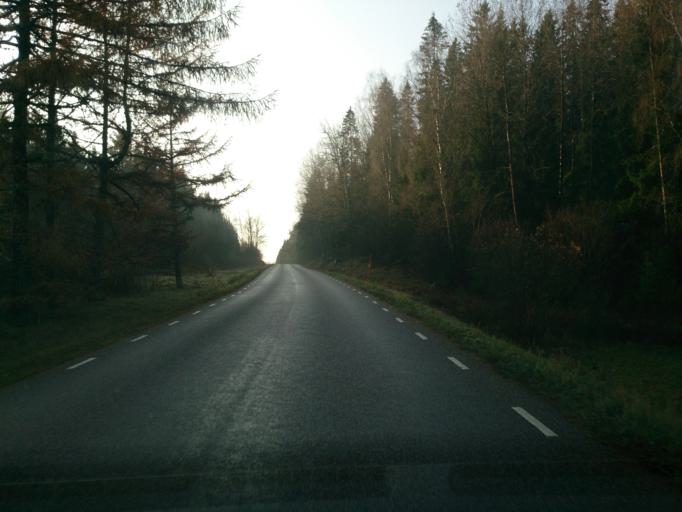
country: SE
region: OEstergoetland
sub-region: Atvidabergs Kommun
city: Atvidaberg
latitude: 58.2997
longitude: 16.0109
